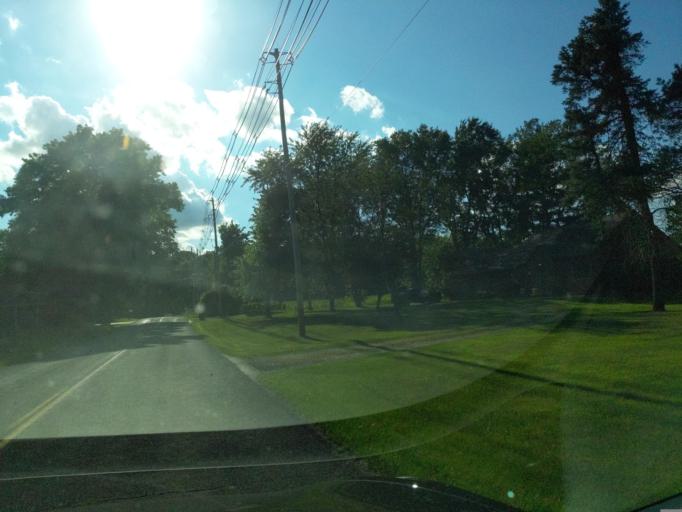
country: US
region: Michigan
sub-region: Ingham County
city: Mason
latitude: 42.5750
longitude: -84.4704
